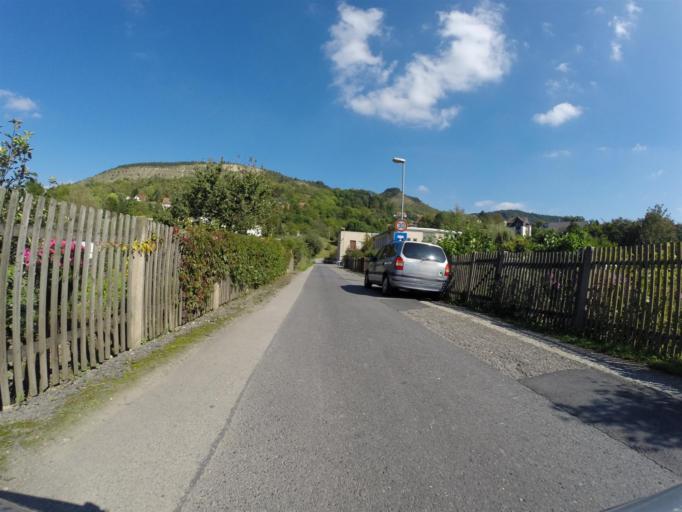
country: DE
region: Thuringia
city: Sulza
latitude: 50.8950
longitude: 11.6033
